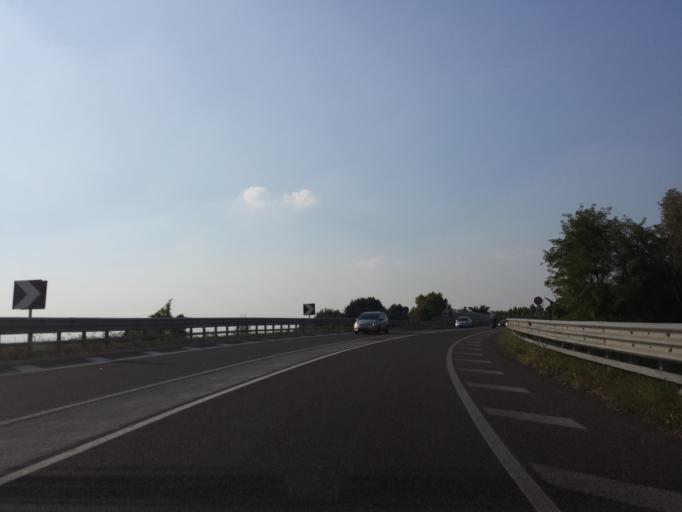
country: IT
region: Veneto
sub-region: Provincia di Vicenza
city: Grumolo delle Abbadesse
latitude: 45.4913
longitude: 11.6641
